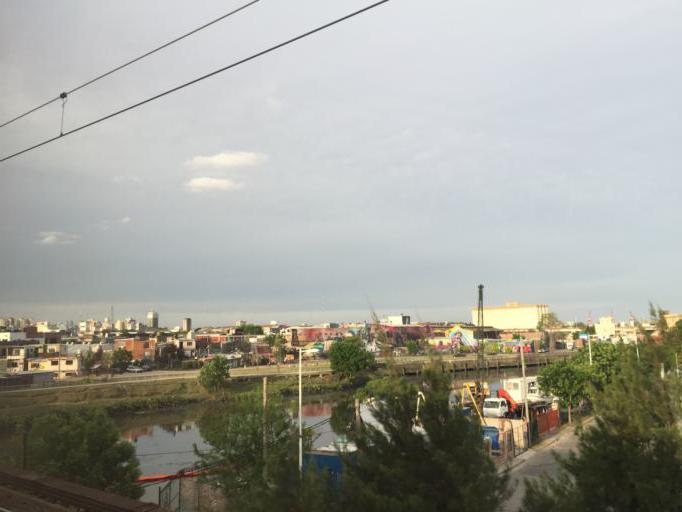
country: AR
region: Buenos Aires
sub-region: Partido de Avellaneda
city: Avellaneda
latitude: -34.6580
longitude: -58.3775
